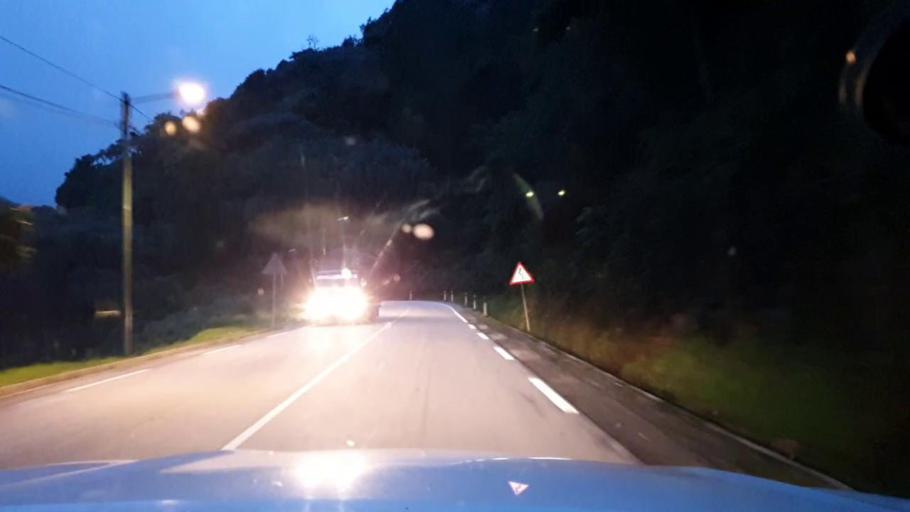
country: RW
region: Southern Province
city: Nzega
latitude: -2.5333
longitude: 29.3871
